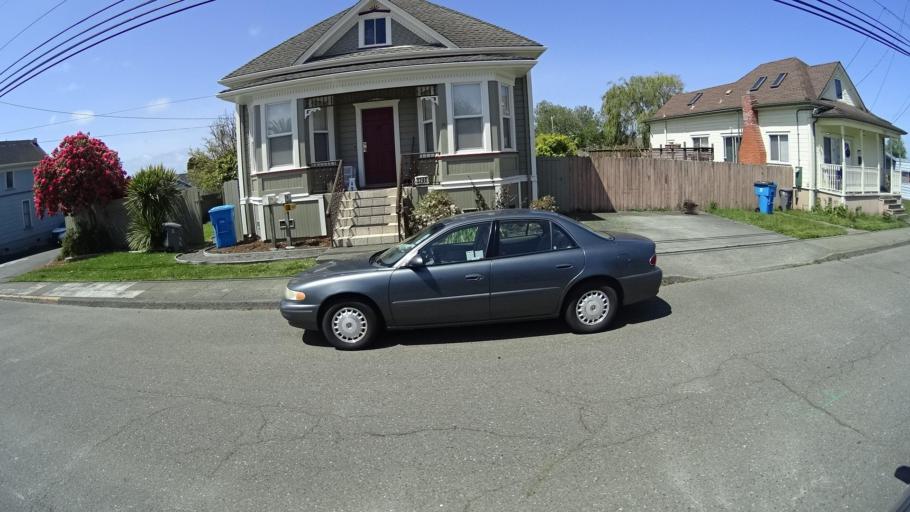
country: US
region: California
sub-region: Humboldt County
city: Bayview
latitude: 40.7790
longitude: -124.1748
